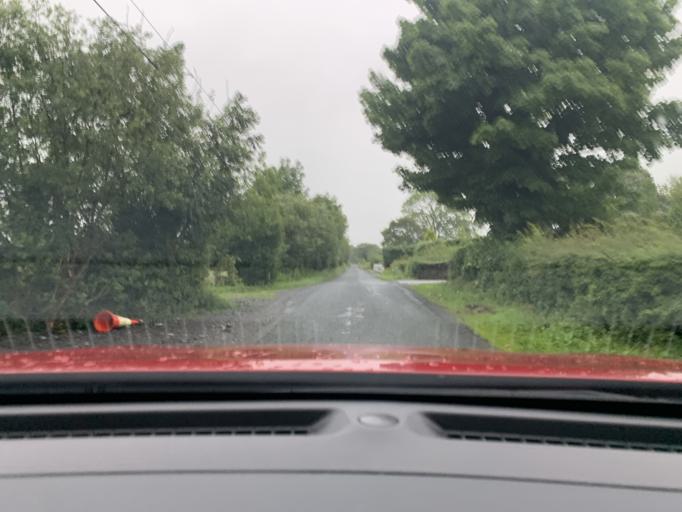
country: IE
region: Connaught
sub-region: Sligo
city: Sligo
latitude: 54.3201
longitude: -8.4752
